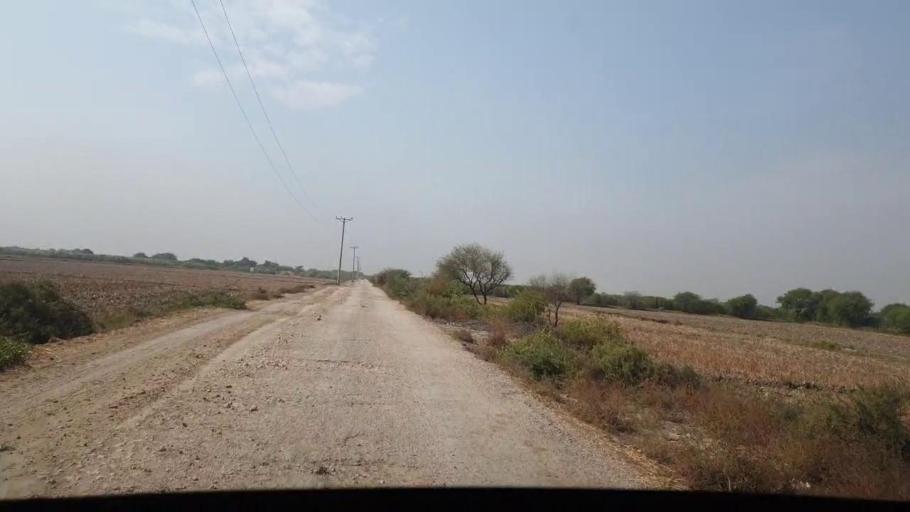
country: PK
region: Sindh
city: Chuhar Jamali
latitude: 24.2741
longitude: 67.9126
